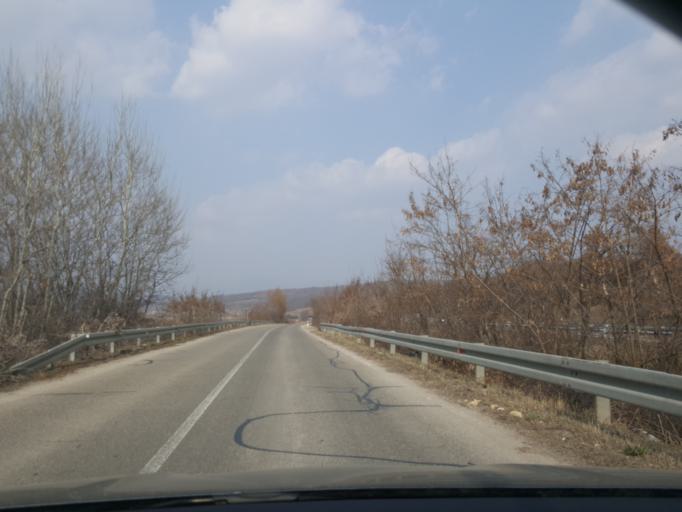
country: RS
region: Central Serbia
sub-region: Nisavski Okrug
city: Aleksinac
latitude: 43.4267
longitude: 21.7970
